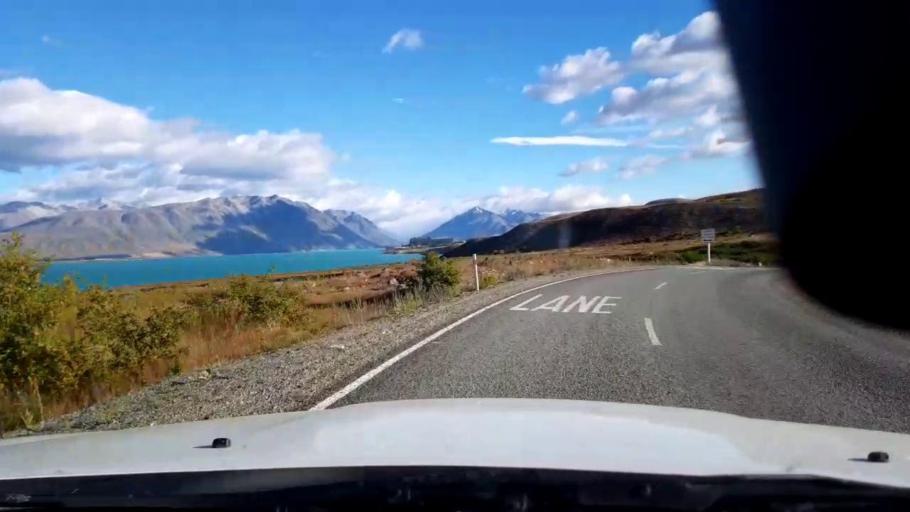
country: NZ
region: Canterbury
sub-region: Timaru District
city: Pleasant Point
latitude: -43.9140
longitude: 170.5574
